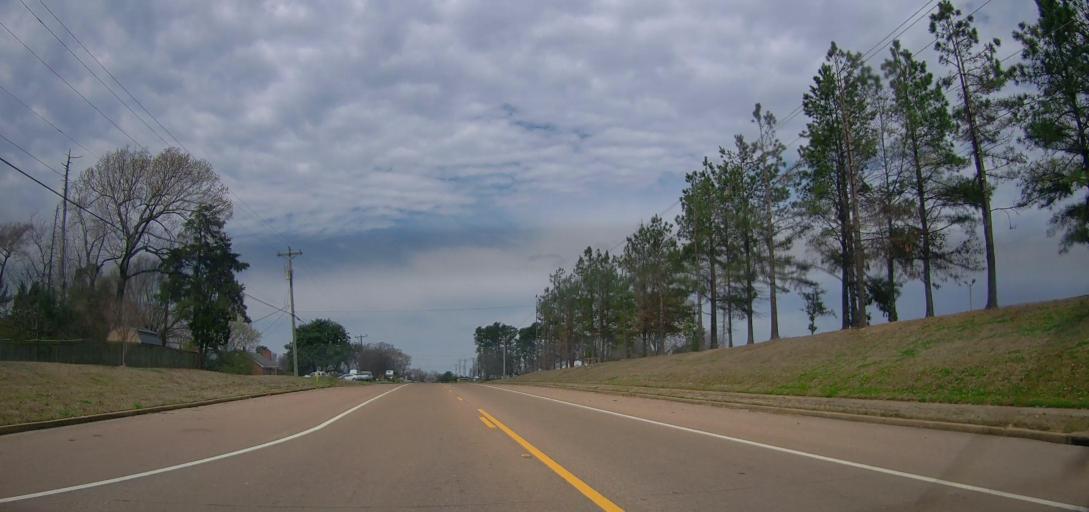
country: US
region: Mississippi
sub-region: De Soto County
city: Olive Branch
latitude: 34.9790
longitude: -89.8523
